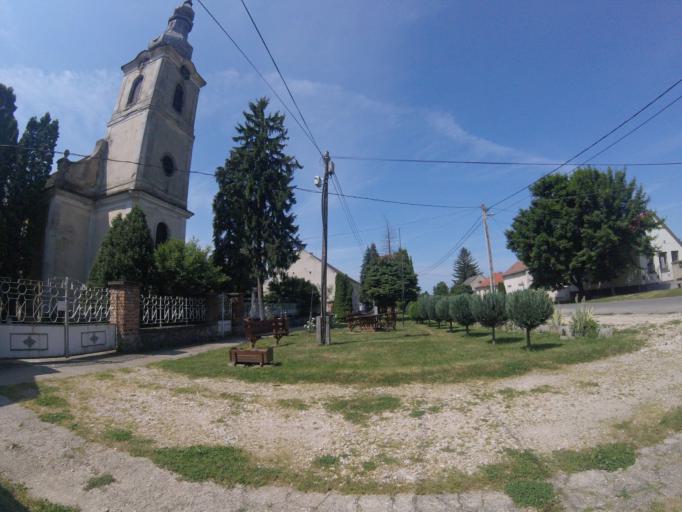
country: HU
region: Baranya
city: Harkany
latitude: 45.8764
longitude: 18.1609
